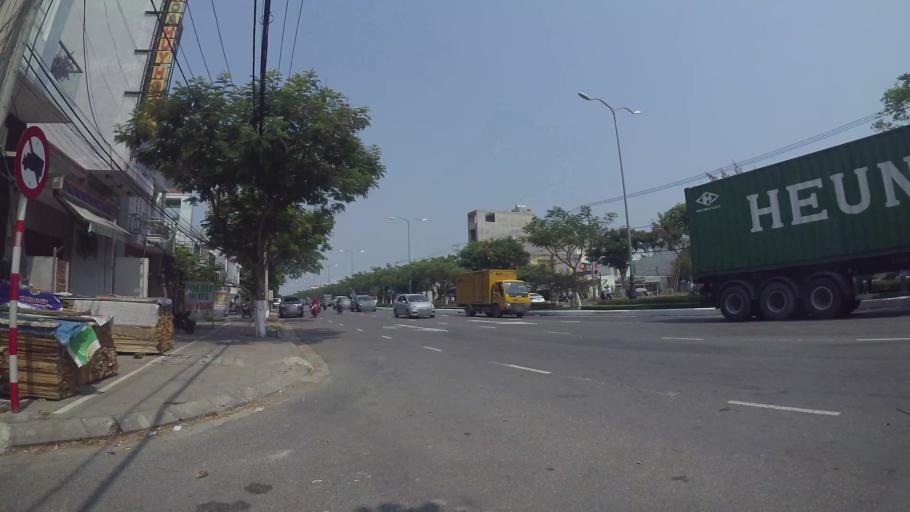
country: VN
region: Da Nang
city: Ngu Hanh Son
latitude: 16.0204
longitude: 108.2519
